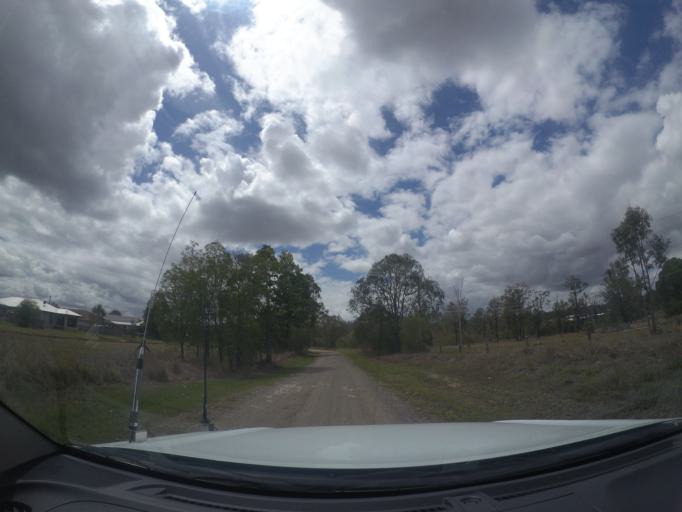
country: AU
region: Queensland
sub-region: Logan
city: Cedar Vale
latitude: -27.8302
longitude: 153.0340
